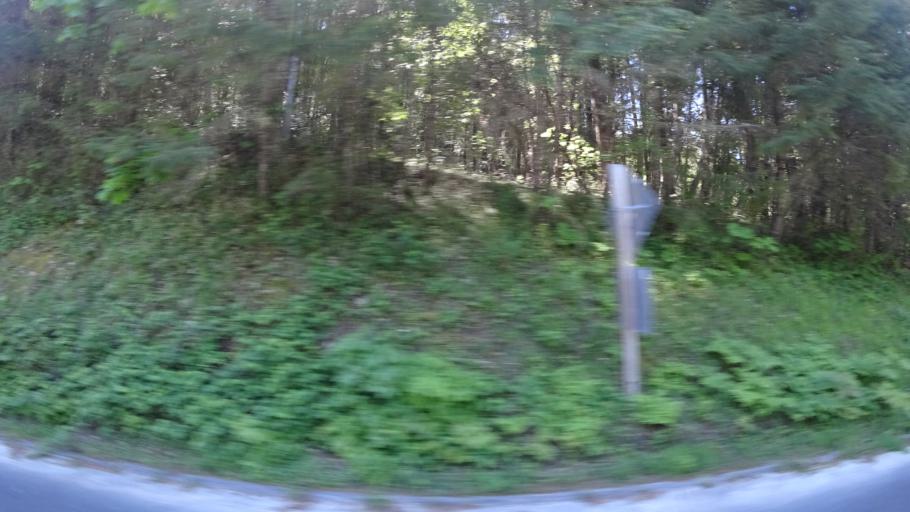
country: US
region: California
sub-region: Humboldt County
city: Willow Creek
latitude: 40.8769
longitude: -123.5380
